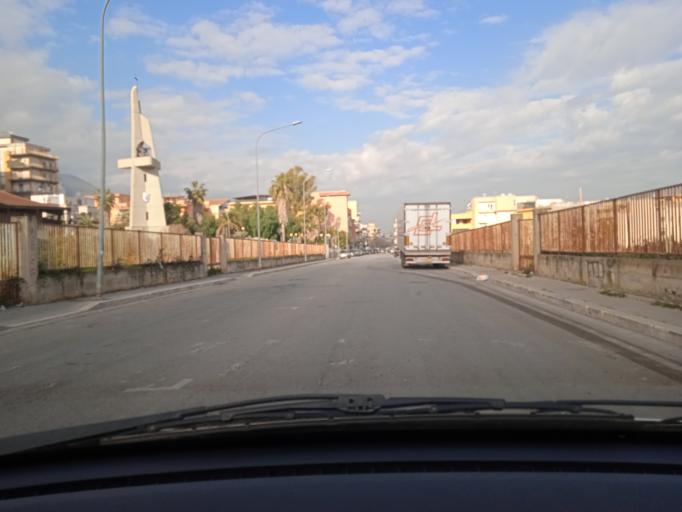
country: IT
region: Sicily
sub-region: Palermo
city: Villabate
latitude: 38.0771
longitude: 13.4500
